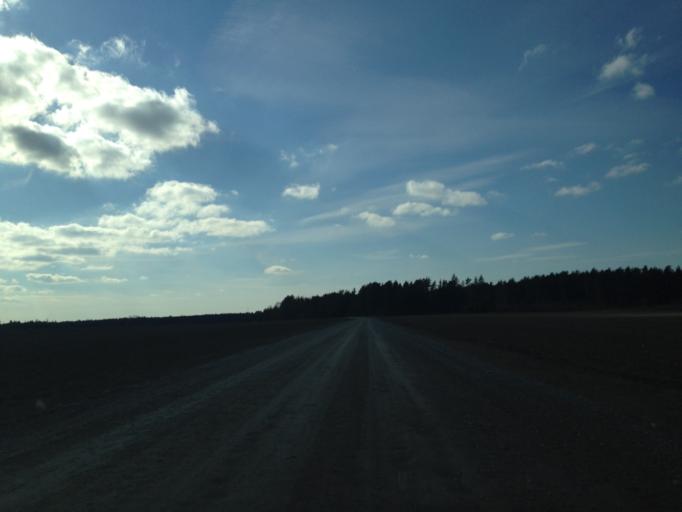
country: EE
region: Harju
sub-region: Nissi vald
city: Riisipere
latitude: 59.1247
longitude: 24.3783
